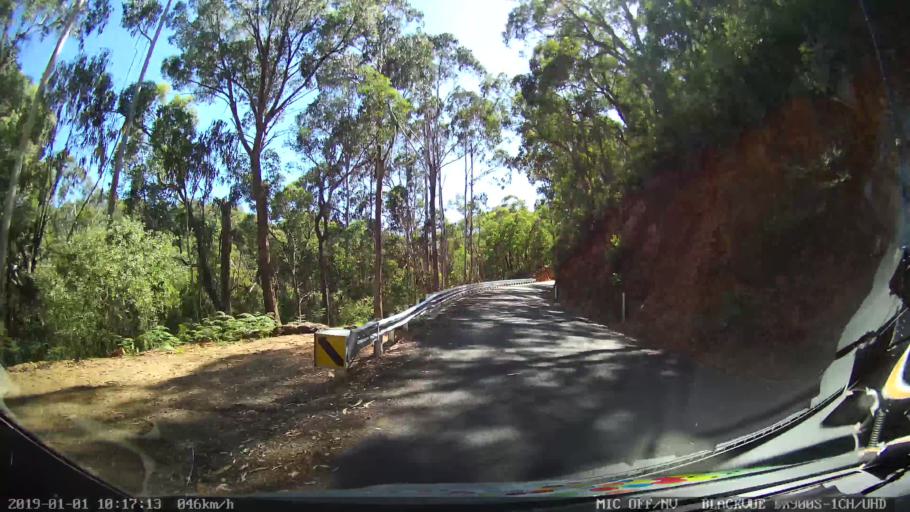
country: AU
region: New South Wales
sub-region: Snowy River
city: Jindabyne
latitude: -36.0912
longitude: 148.1742
